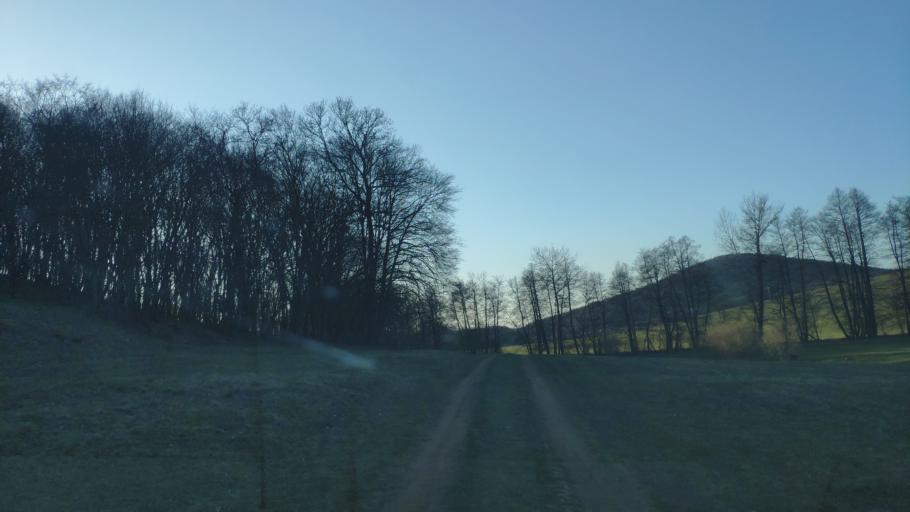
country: HU
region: Borsod-Abauj-Zemplen
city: Putnok
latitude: 48.5170
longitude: 20.3230
